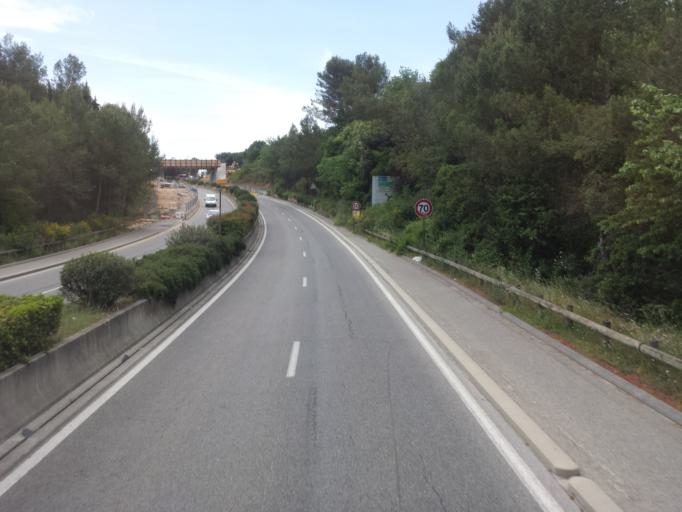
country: FR
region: Provence-Alpes-Cote d'Azur
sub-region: Departement des Alpes-Maritimes
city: Biot
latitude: 43.6076
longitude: 7.0818
